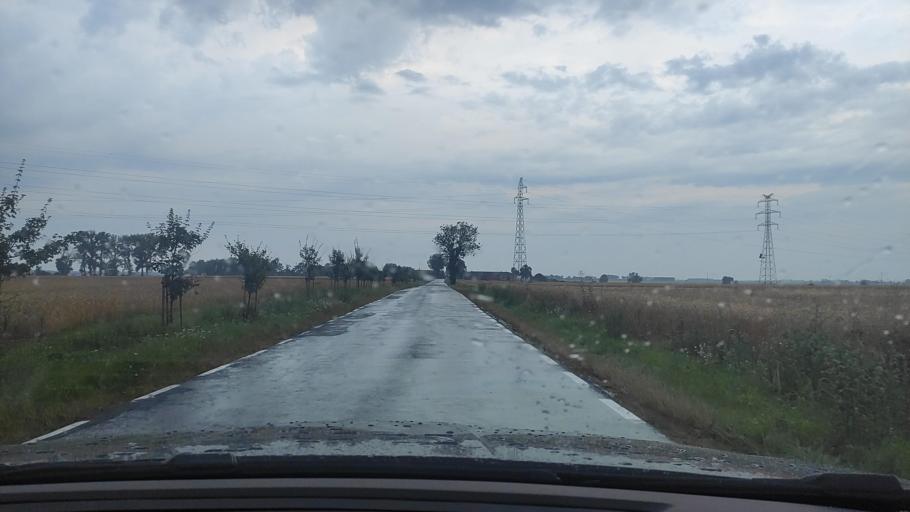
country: PL
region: Greater Poland Voivodeship
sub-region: Powiat poznanski
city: Kleszczewo
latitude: 52.2924
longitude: 17.1709
